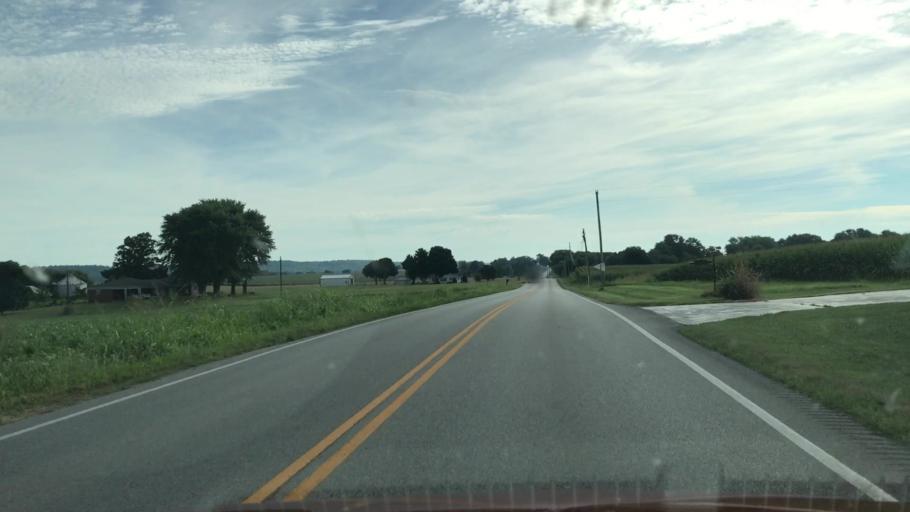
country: US
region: Kentucky
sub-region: Edmonson County
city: Brownsville
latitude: 37.0517
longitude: -86.3093
